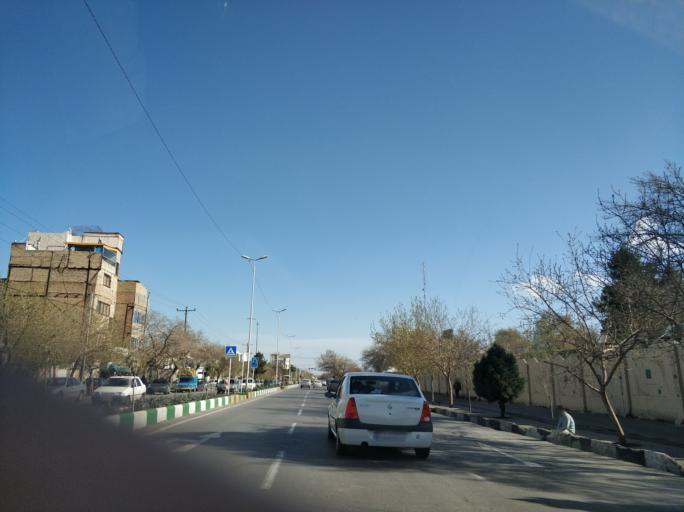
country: IR
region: Razavi Khorasan
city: Mashhad
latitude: 36.3008
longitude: 59.6321
